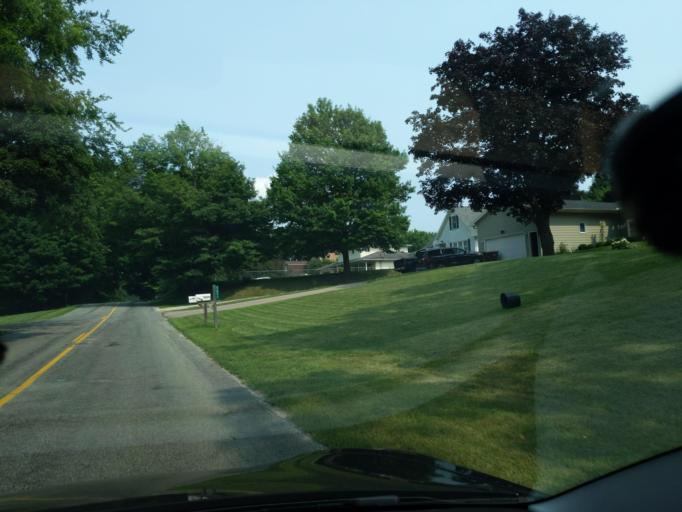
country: US
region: Michigan
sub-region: Ingham County
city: Holt
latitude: 42.6113
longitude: -84.5695
